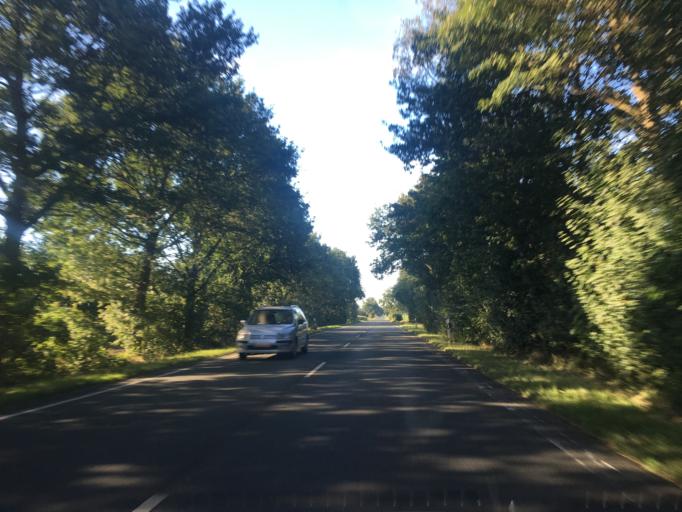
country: DE
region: North Rhine-Westphalia
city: Olfen
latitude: 51.7457
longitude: 7.3291
